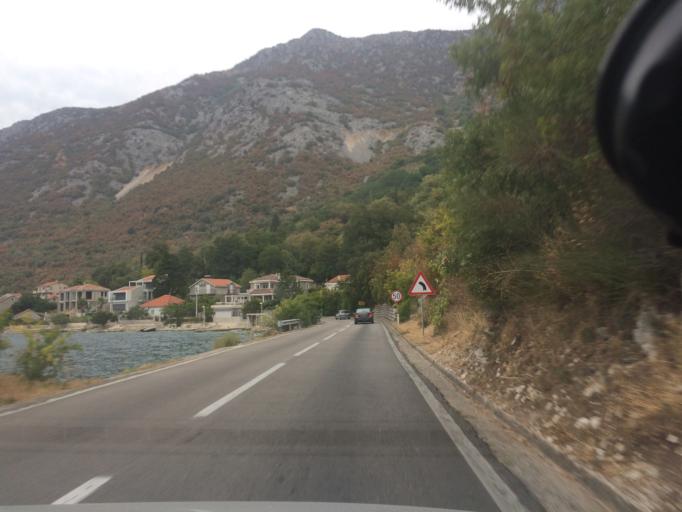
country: ME
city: Lipci
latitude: 42.5049
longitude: 18.6742
